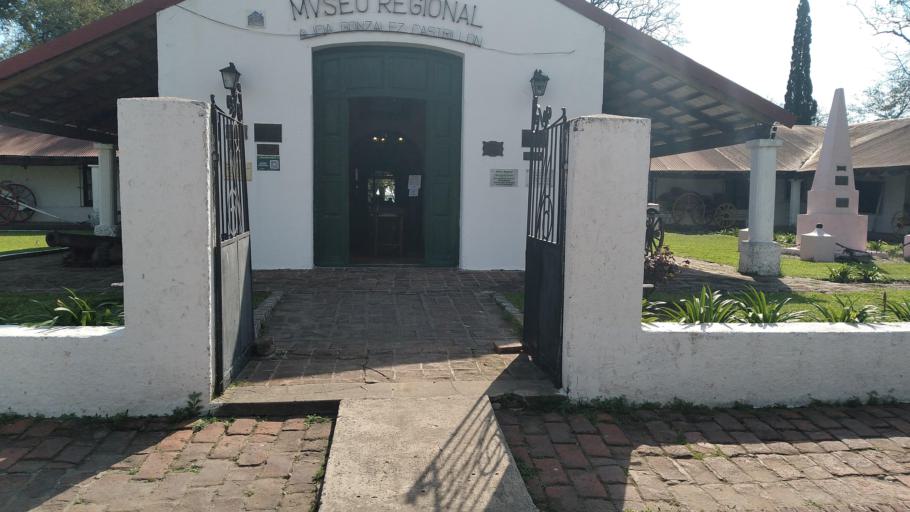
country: AR
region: Entre Rios
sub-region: Departamento de La Paz
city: La Paz
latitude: -30.7377
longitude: -59.6454
